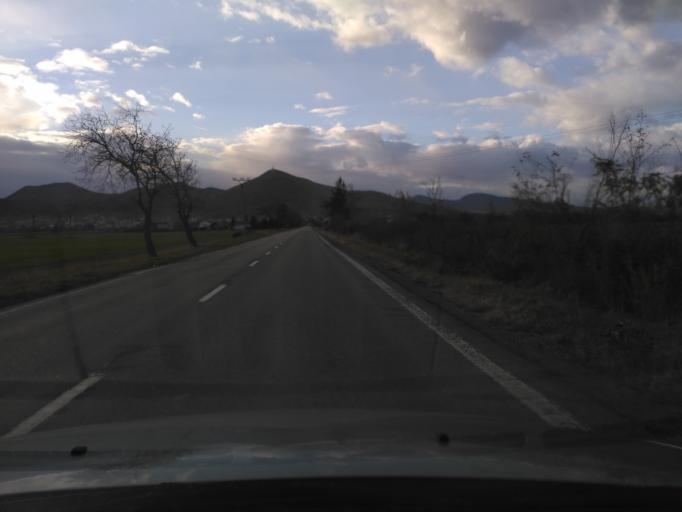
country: HU
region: Borsod-Abauj-Zemplen
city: Satoraljaujhely
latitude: 48.3969
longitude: 21.6916
